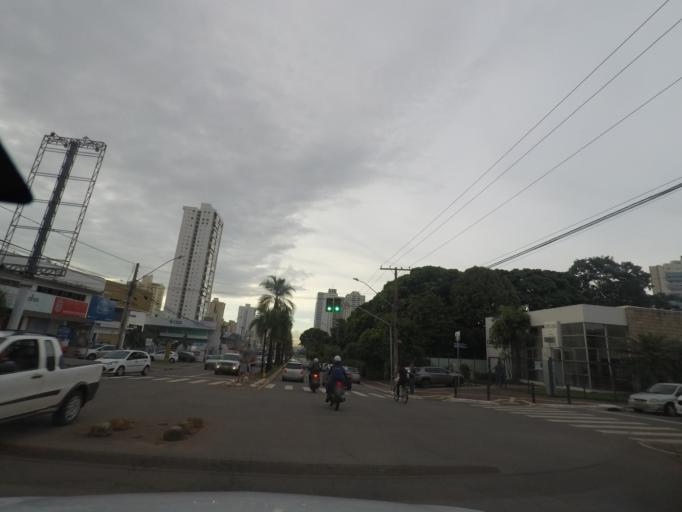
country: BR
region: Goias
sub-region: Goiania
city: Goiania
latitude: -16.6940
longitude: -49.2725
